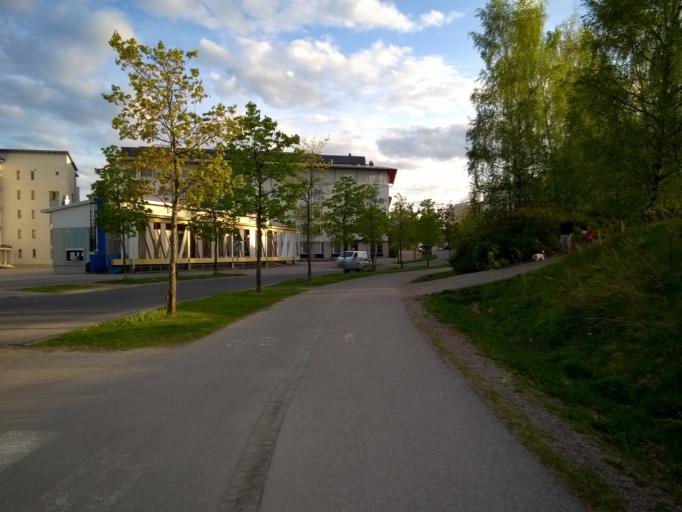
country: FI
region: Uusimaa
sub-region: Helsinki
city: Vantaa
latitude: 60.2278
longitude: 25.0274
